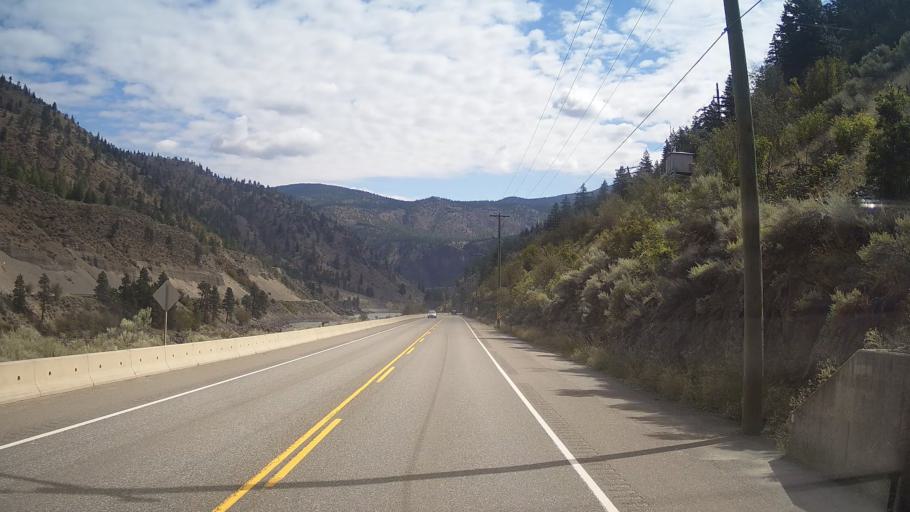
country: CA
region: British Columbia
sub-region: Thompson-Nicola Regional District
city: Ashcroft
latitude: 50.2585
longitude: -121.4312
